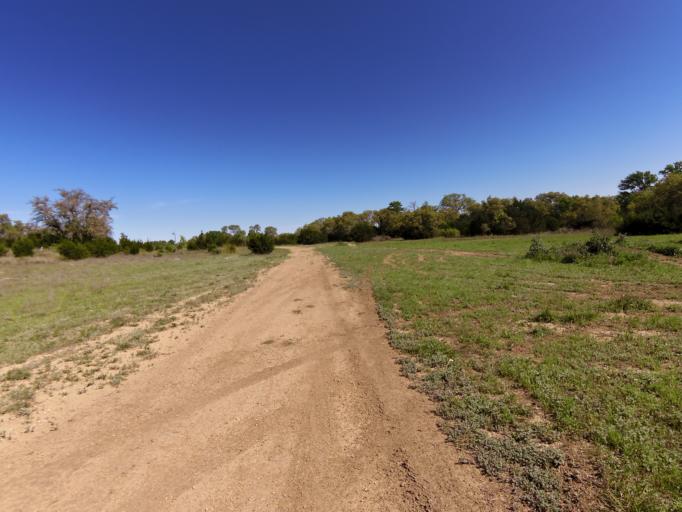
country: US
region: Texas
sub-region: Bexar County
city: Cross Mountain
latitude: 29.6777
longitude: -98.6424
